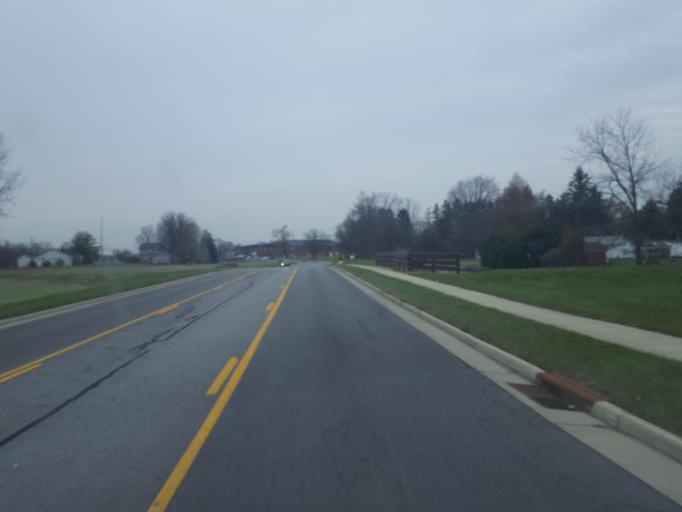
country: US
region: Ohio
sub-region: Marion County
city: Marion
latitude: 40.5872
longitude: -83.0905
